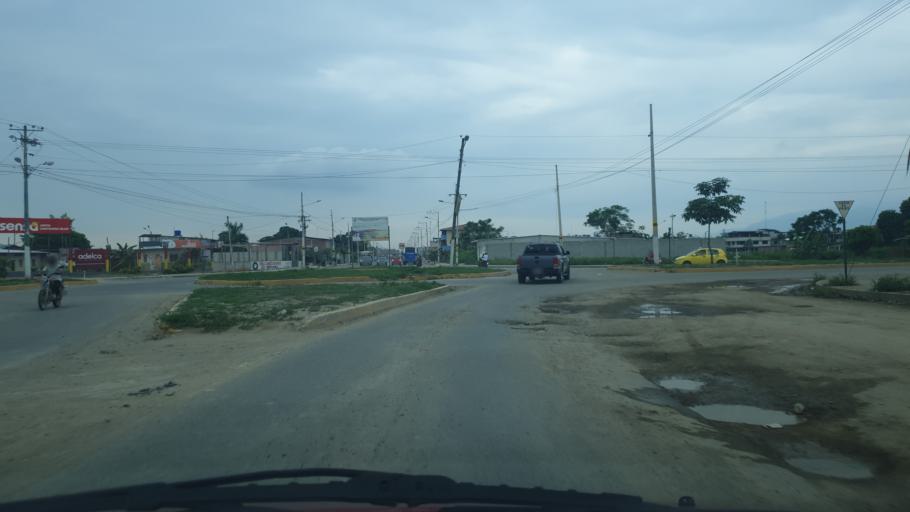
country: EC
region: El Oro
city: Pasaje
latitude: -3.3418
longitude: -79.8146
